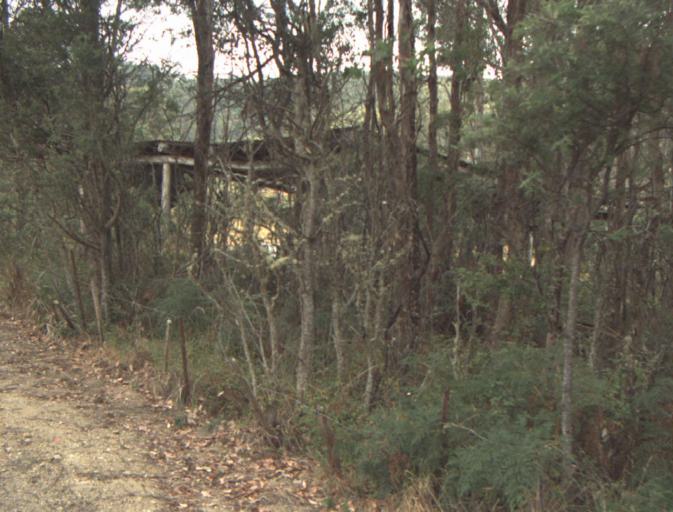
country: AU
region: Tasmania
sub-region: Northern Midlands
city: Evandale
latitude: -41.4585
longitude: 147.4466
